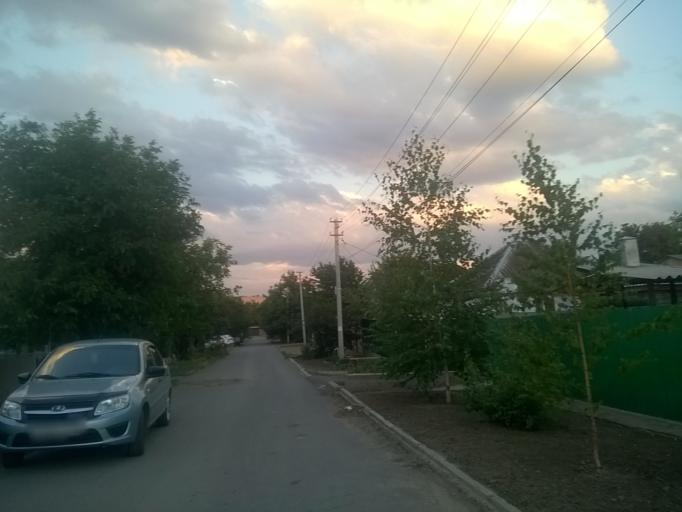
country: RU
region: Rostov
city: Donetsk
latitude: 48.3333
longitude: 39.9564
